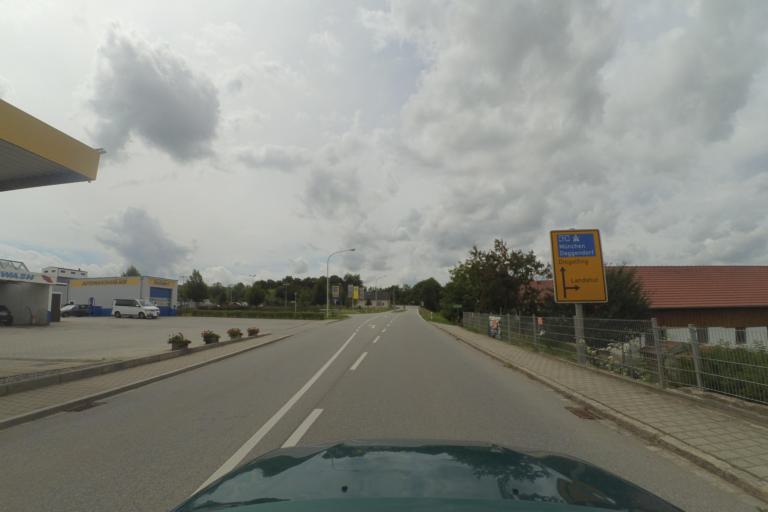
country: DE
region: Bavaria
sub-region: Lower Bavaria
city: Mengkofen
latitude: 48.7149
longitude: 12.4308
